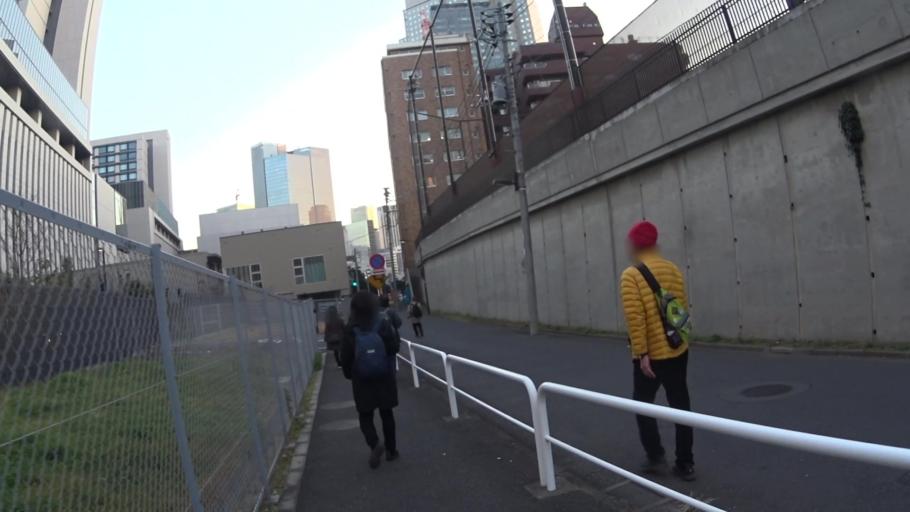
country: JP
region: Tokyo
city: Tokyo
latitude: 35.6763
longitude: 139.7415
